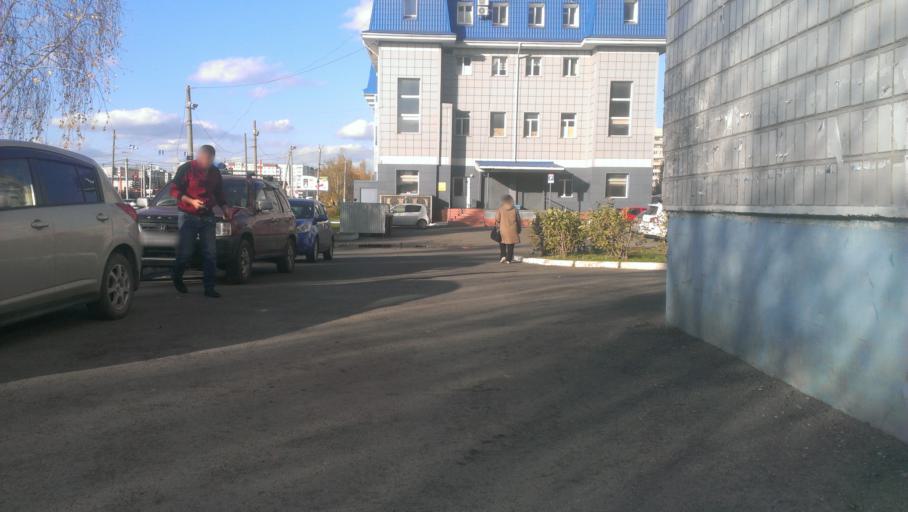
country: RU
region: Altai Krai
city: Novosilikatnyy
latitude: 53.3349
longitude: 83.6694
